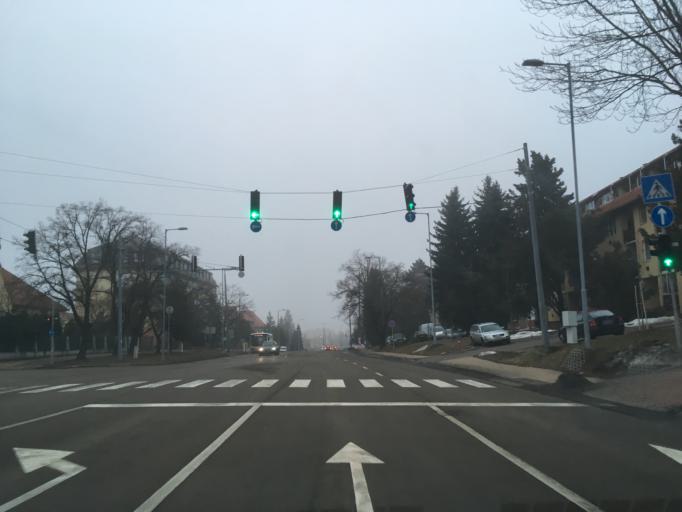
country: HU
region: Heves
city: Eger
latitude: 47.8933
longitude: 20.3772
